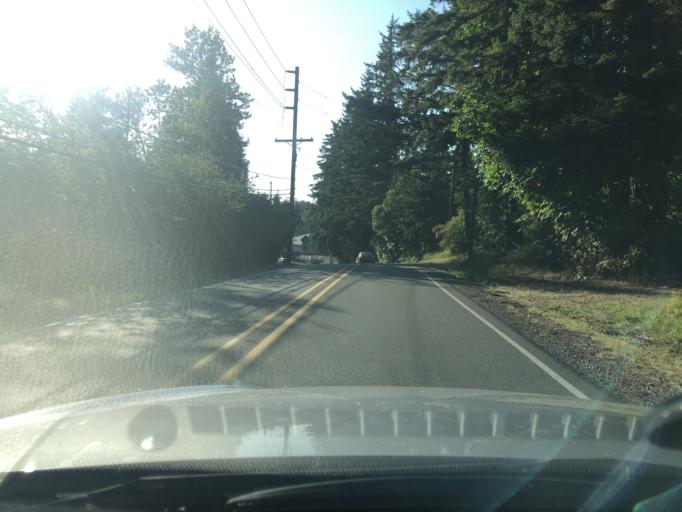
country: US
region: Washington
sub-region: King County
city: Pacific
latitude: 47.2496
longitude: -122.1826
